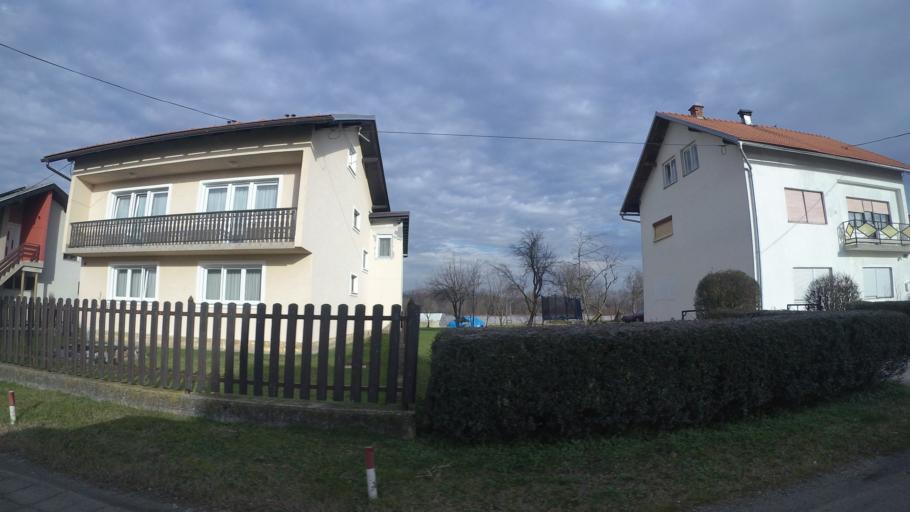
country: HR
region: Karlovacka
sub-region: Grad Karlovac
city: Karlovac
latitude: 45.4619
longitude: 15.5542
